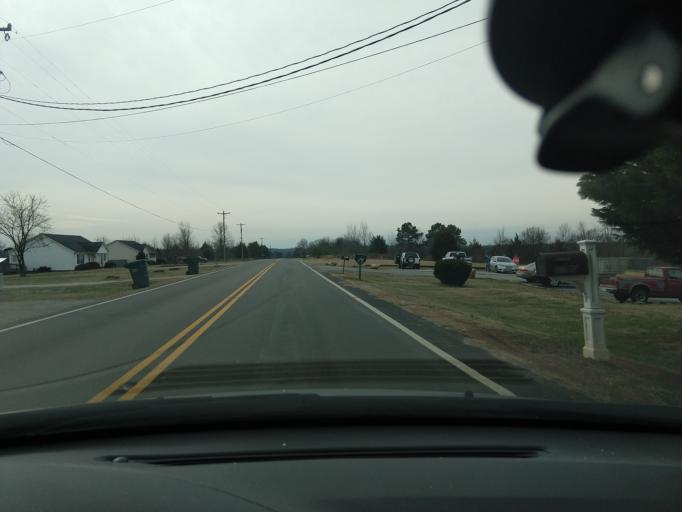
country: US
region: South Carolina
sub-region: Spartanburg County
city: Cowpens
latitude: 35.0526
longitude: -81.7877
